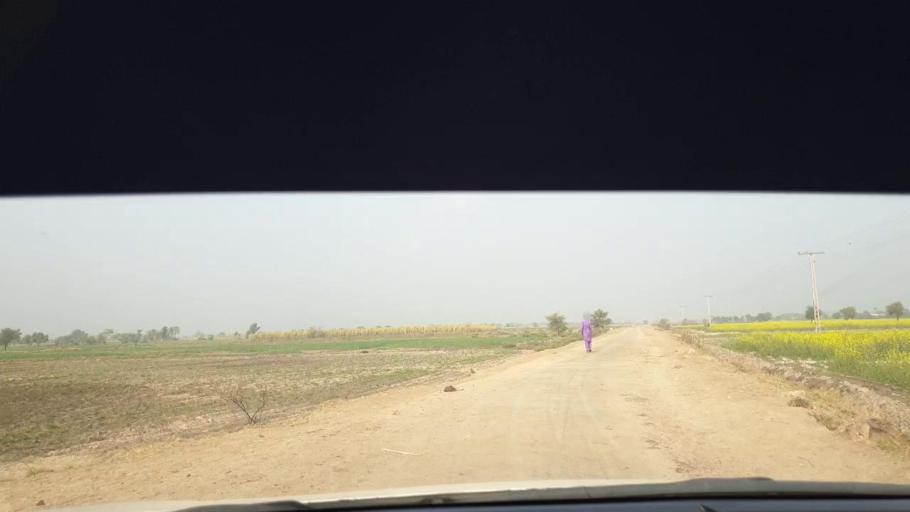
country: PK
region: Sindh
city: Berani
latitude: 25.8310
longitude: 68.8480
